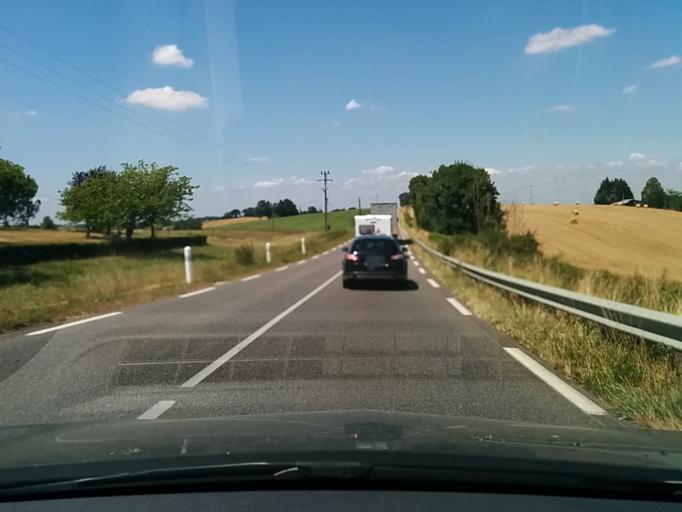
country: FR
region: Midi-Pyrenees
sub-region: Departement du Gers
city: Eauze
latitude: 43.7738
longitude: 0.1250
